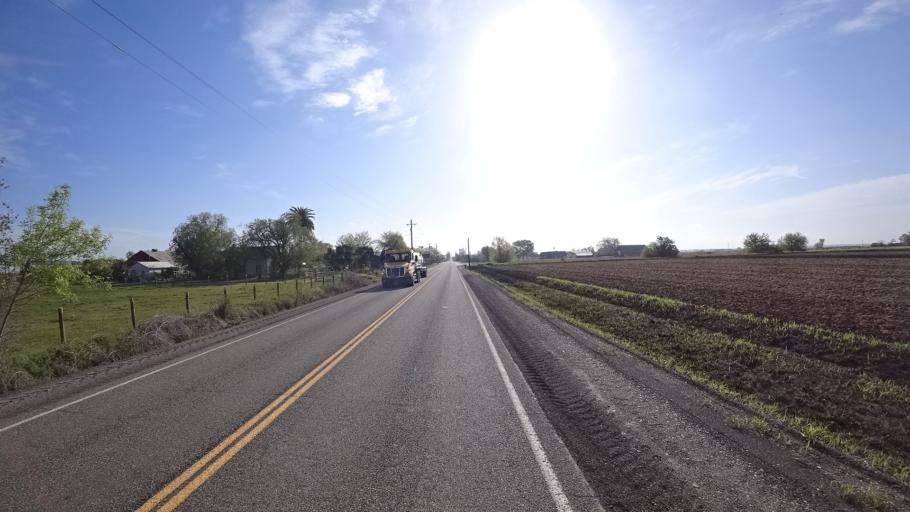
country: US
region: California
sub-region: Glenn County
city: Willows
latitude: 39.5825
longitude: -122.0503
